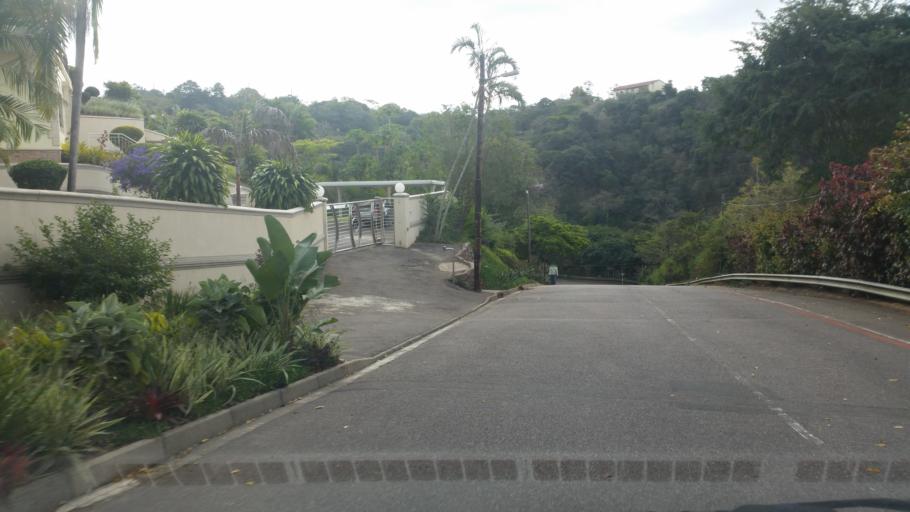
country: ZA
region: KwaZulu-Natal
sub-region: eThekwini Metropolitan Municipality
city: Berea
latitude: -29.8257
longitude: 30.9262
